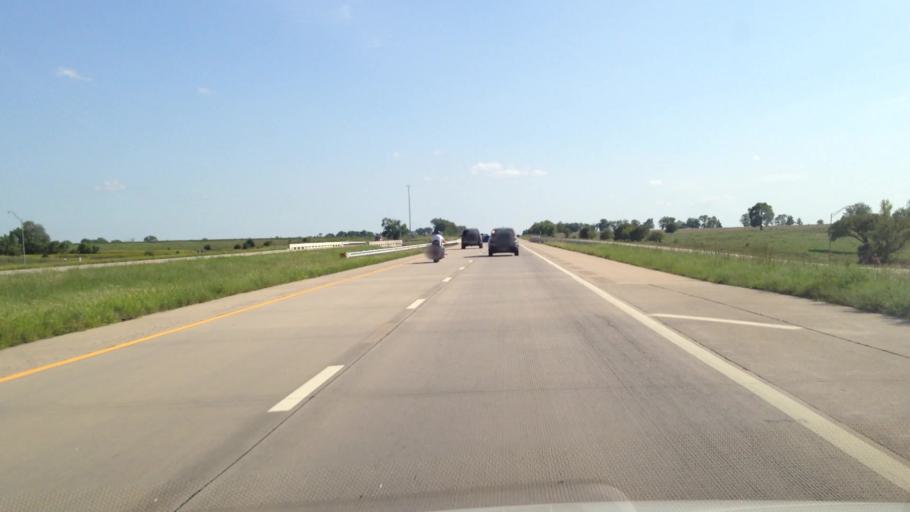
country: US
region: Kansas
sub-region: Bourbon County
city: Fort Scott
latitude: 37.9954
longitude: -94.7051
